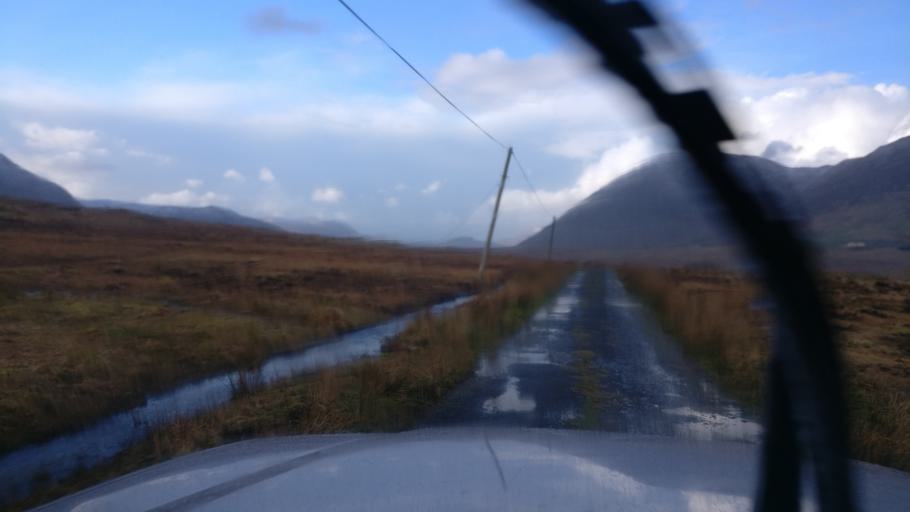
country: IE
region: Connaught
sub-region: County Galway
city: Clifden
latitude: 53.4970
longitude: -9.7054
